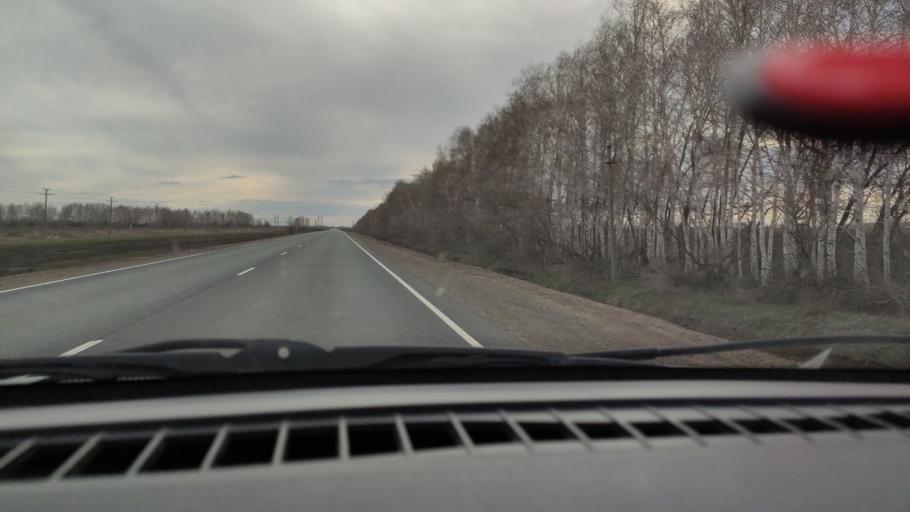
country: RU
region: Bashkortostan
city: Mayachnyy
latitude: 52.3745
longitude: 55.6307
